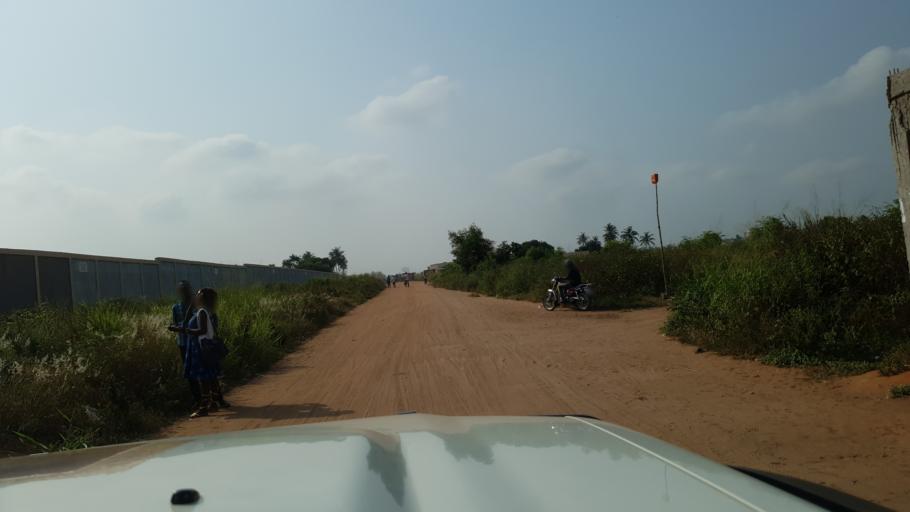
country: TG
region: Maritime
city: Lome
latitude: 6.1716
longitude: 1.2099
